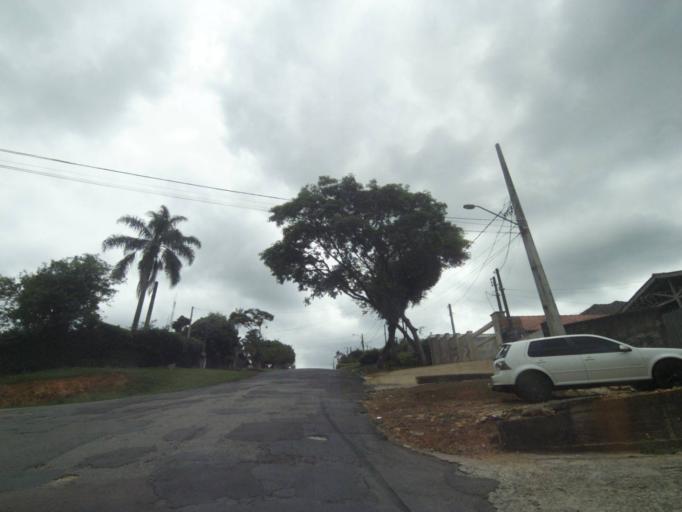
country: BR
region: Parana
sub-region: Curitiba
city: Curitiba
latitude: -25.3911
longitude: -49.2808
